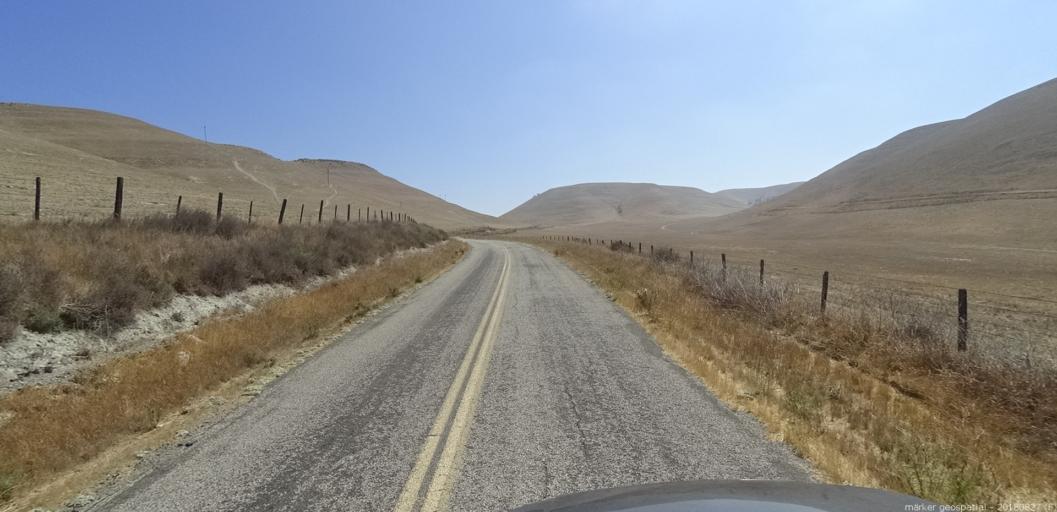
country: US
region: California
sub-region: Monterey County
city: King City
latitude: 36.2465
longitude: -121.0291
